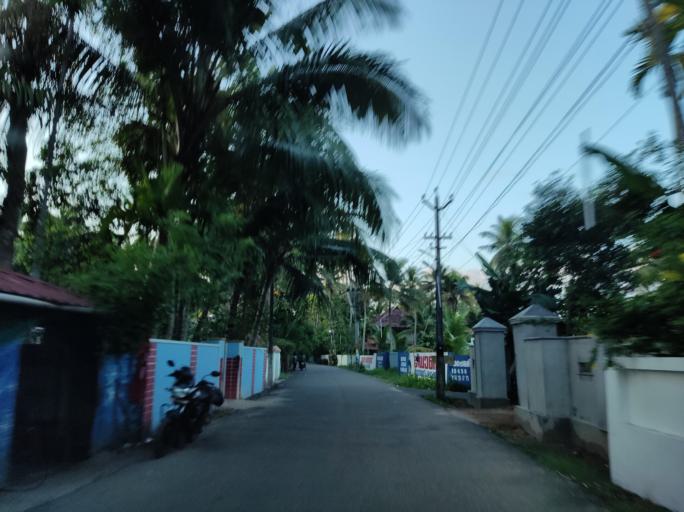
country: IN
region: Kerala
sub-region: Alappuzha
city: Vayalar
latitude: 9.7153
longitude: 76.2973
